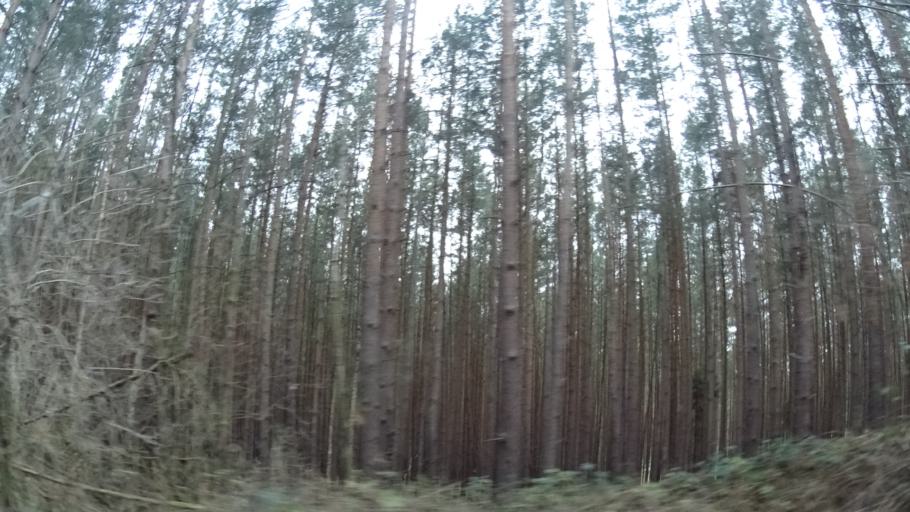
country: DE
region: Thuringia
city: Reinstadt
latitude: 50.7571
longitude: 11.4539
